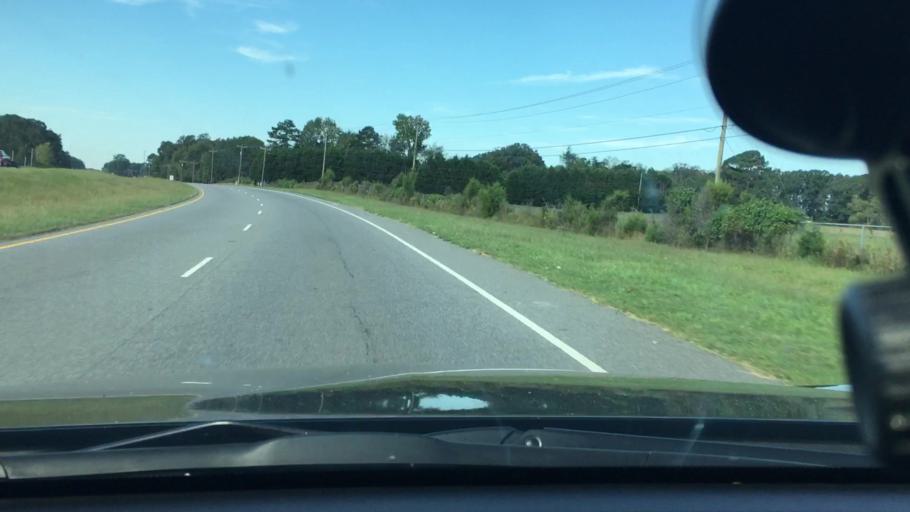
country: US
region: North Carolina
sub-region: Cabarrus County
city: Midland
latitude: 35.2558
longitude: -80.4770
